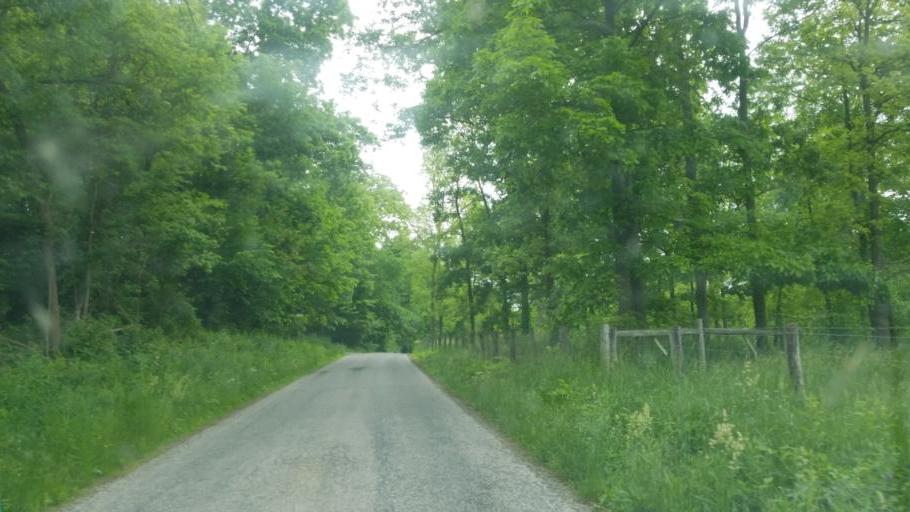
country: US
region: Ohio
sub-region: Wayne County
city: Apple Creek
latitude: 40.6327
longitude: -81.7396
